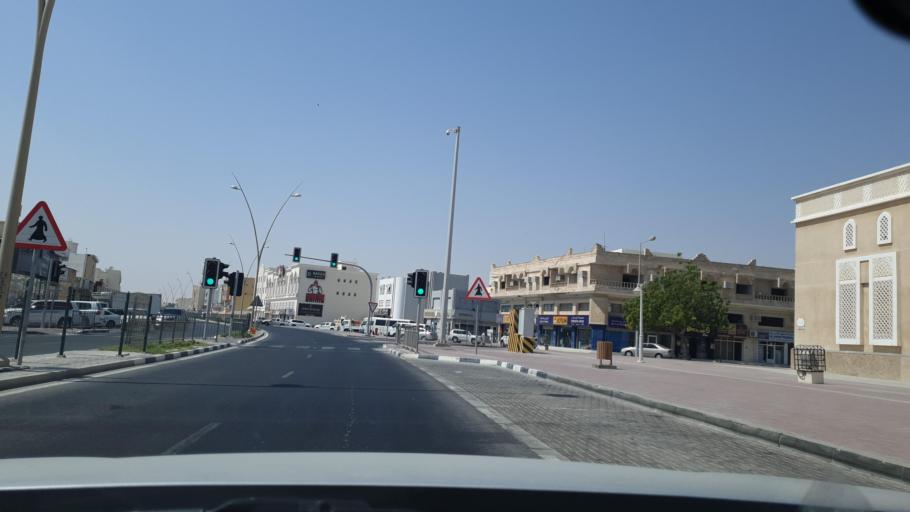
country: QA
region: Al Khawr
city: Al Khawr
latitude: 25.6843
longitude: 51.5069
